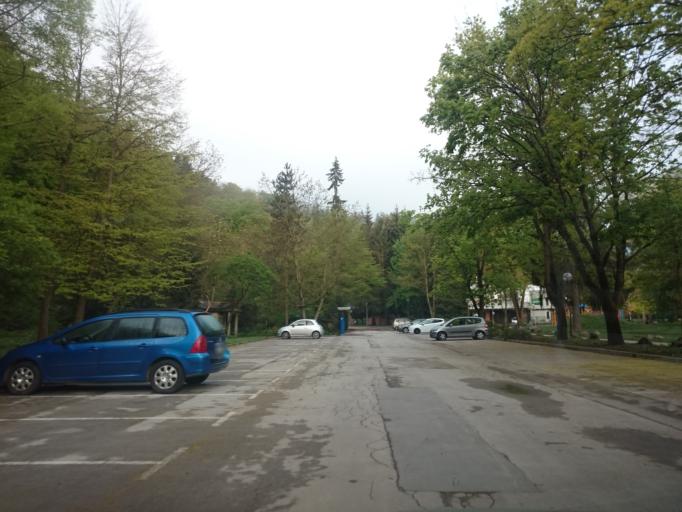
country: SI
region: Celje
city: Celje
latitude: 46.2255
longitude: 15.2627
